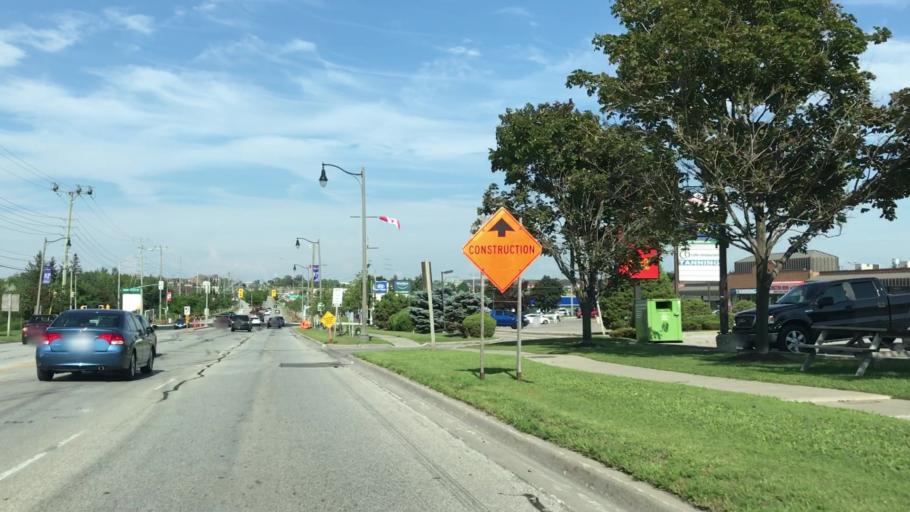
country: CA
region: Ontario
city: Newmarket
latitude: 44.0029
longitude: -79.4526
